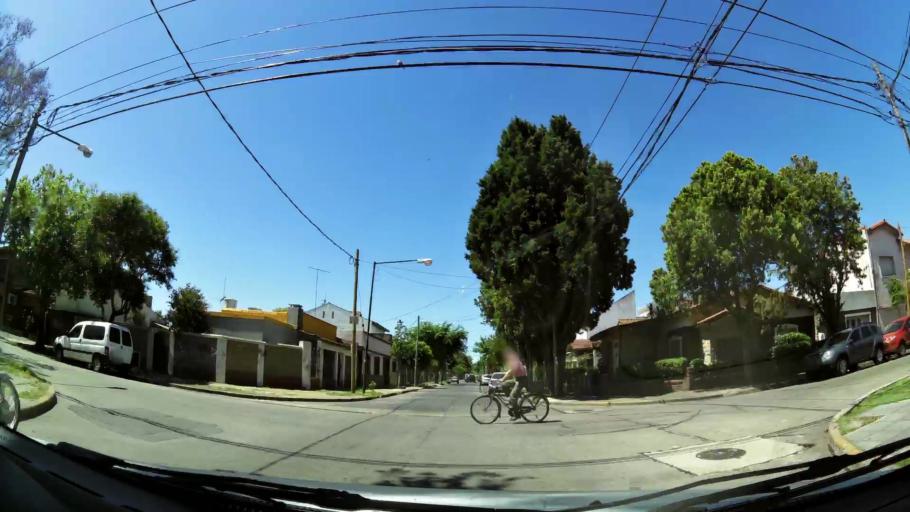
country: AR
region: Buenos Aires
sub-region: Partido de General San Martin
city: General San Martin
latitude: -34.5247
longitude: -58.5513
